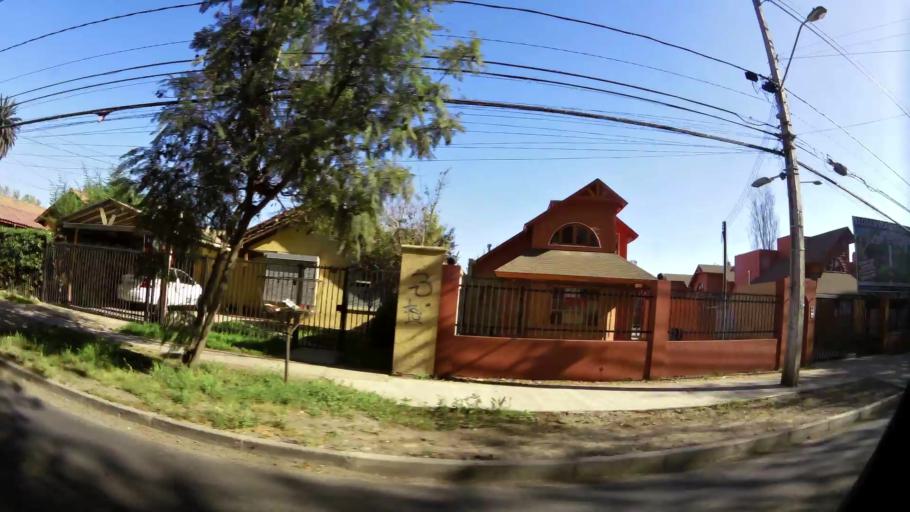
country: CL
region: Santiago Metropolitan
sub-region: Provincia de Talagante
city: Penaflor
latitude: -33.5998
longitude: -70.8691
